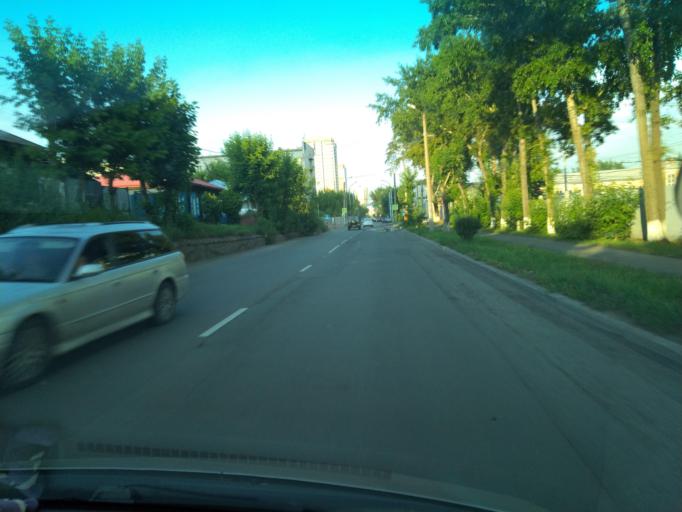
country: RU
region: Krasnoyarskiy
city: Krasnoyarsk
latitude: 56.0312
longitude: 92.9034
